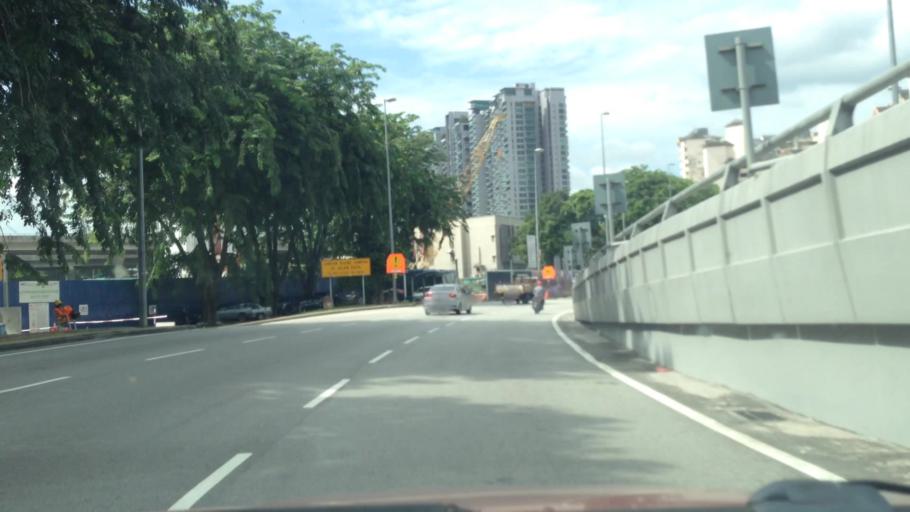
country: MY
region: Kuala Lumpur
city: Kuala Lumpur
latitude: 3.0898
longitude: 101.6928
